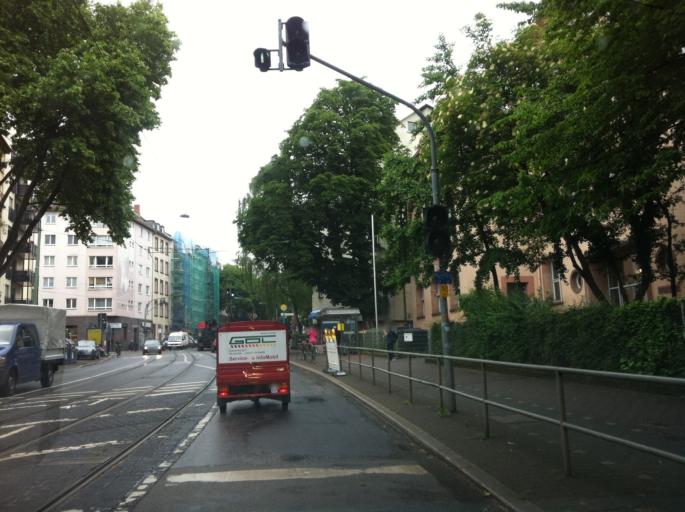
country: DE
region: Hesse
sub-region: Regierungsbezirk Darmstadt
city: Frankfurt am Main
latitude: 50.1176
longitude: 8.7012
